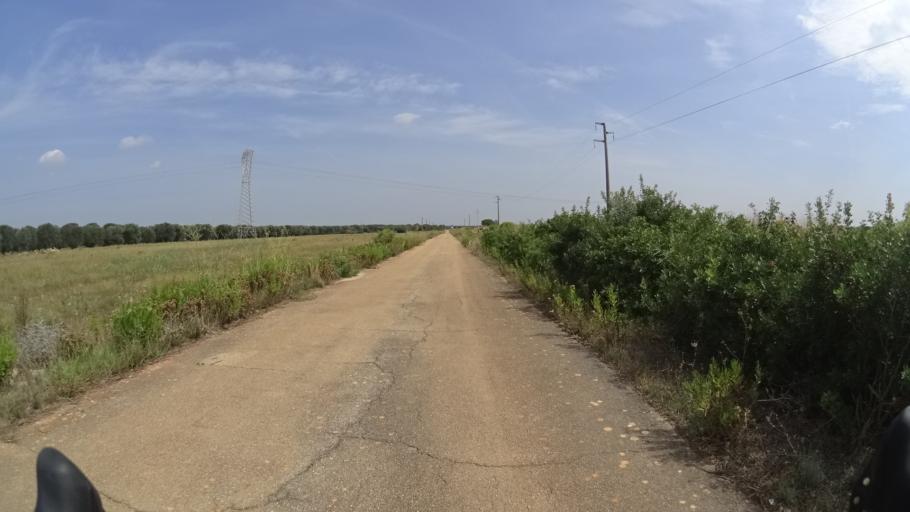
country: IT
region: Apulia
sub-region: Provincia di Brindisi
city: San Pancrazio Salentino
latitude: 40.3454
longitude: 17.8418
